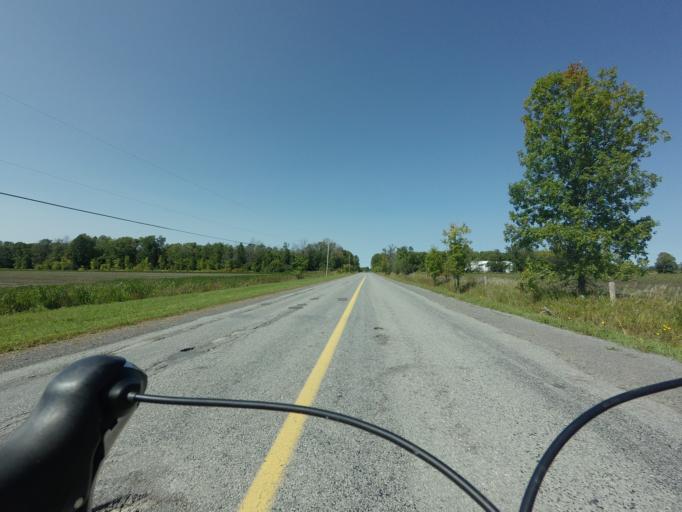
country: CA
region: Ontario
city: Bells Corners
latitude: 45.4308
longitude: -76.0575
